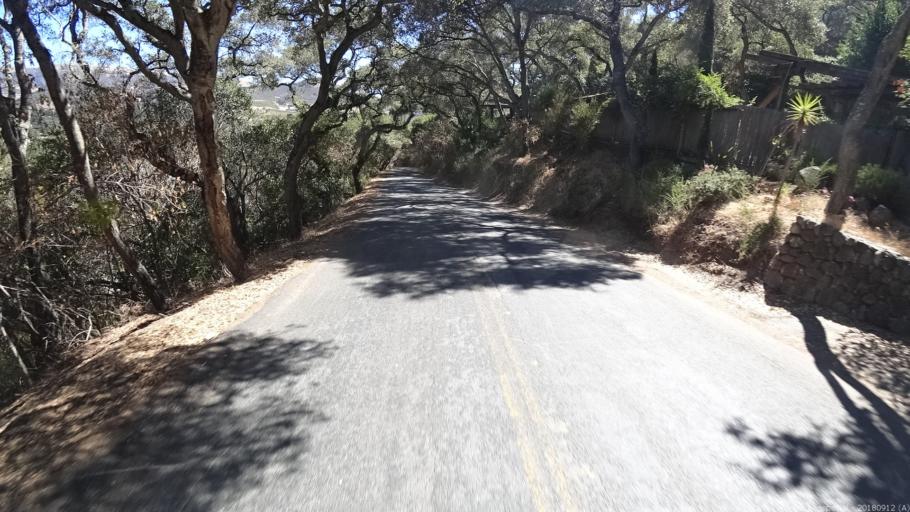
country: US
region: California
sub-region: Monterey County
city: Carmel Valley Village
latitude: 36.4721
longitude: -121.7292
